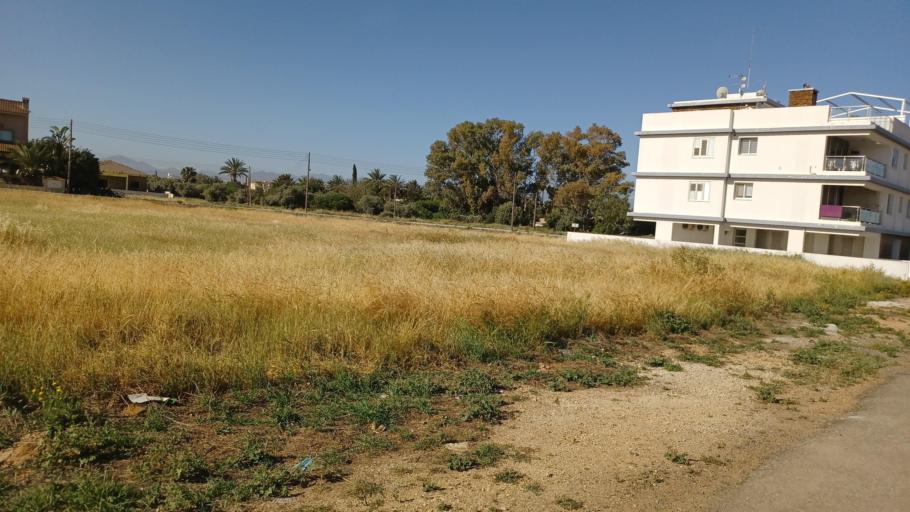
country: CY
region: Lefkosia
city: Kokkinotrimithia
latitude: 35.1509
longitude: 33.1958
